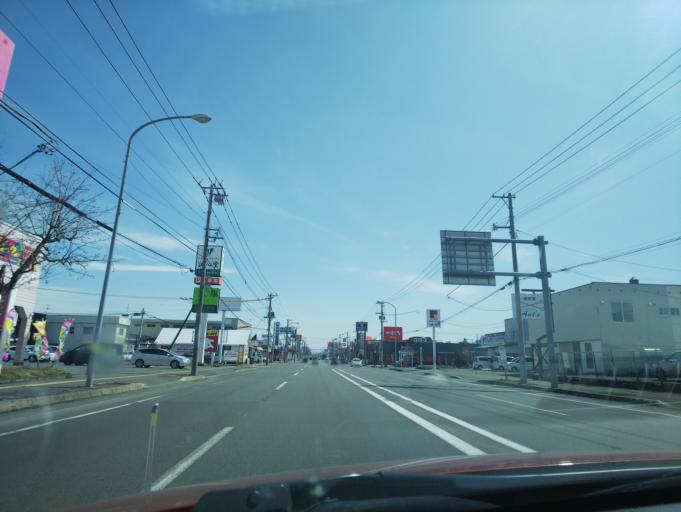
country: JP
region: Hokkaido
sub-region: Asahikawa-shi
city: Asahikawa
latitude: 43.7892
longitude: 142.4065
